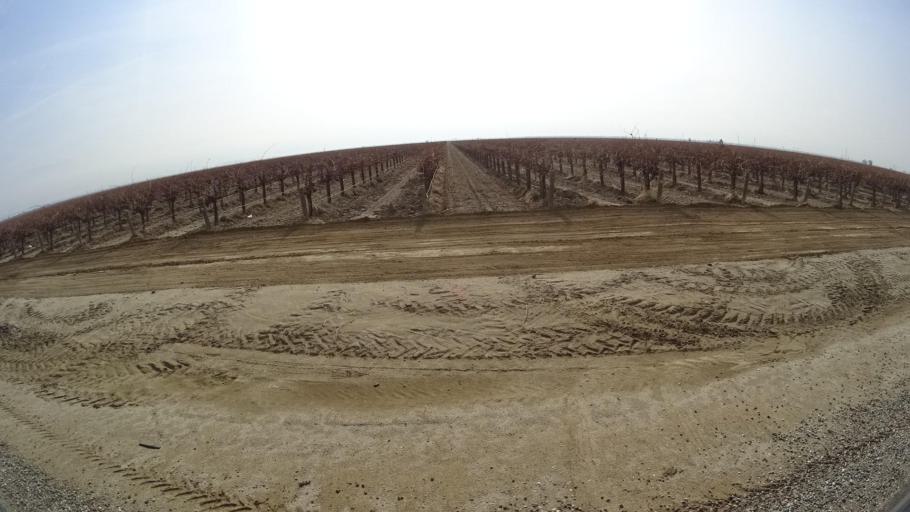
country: US
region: California
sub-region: Kern County
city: Arvin
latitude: 35.0453
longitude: -118.8598
